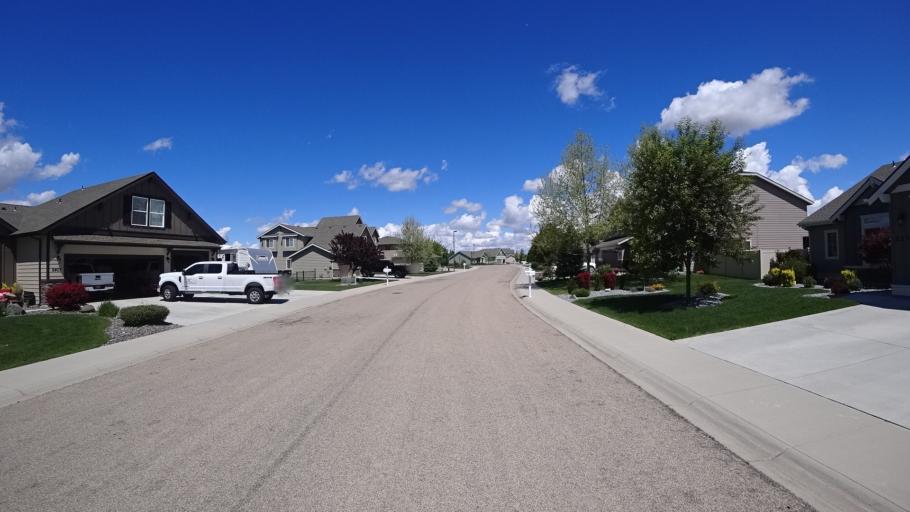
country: US
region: Idaho
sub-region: Ada County
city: Kuna
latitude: 43.5110
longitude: -116.4282
